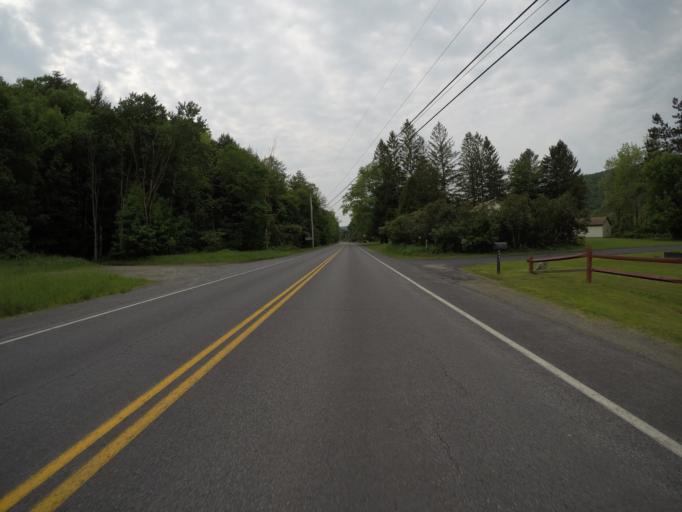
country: US
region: New York
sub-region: Sullivan County
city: Livingston Manor
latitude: 41.9624
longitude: -74.9080
